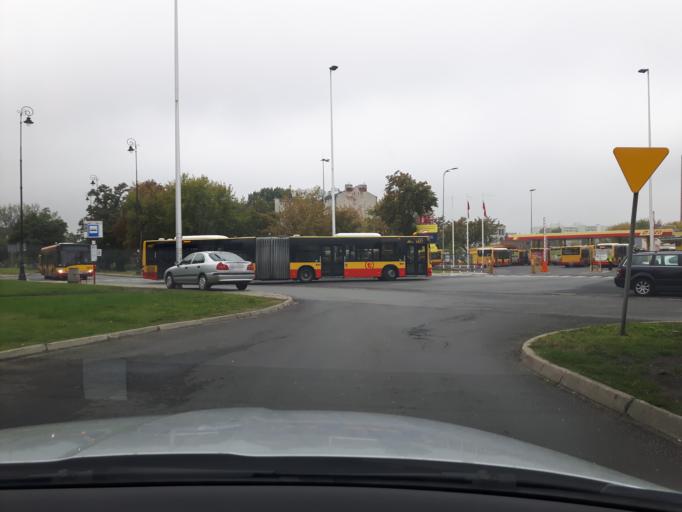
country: PL
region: Masovian Voivodeship
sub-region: Warszawa
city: Praga Polnoc
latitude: 52.2635
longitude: 21.0487
